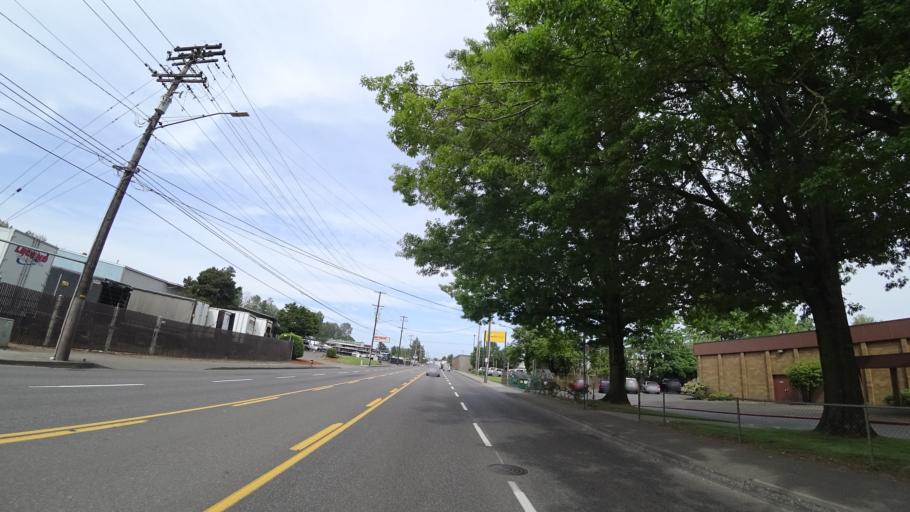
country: US
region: Oregon
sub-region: Multnomah County
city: Portland
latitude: 45.5701
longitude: -122.6098
